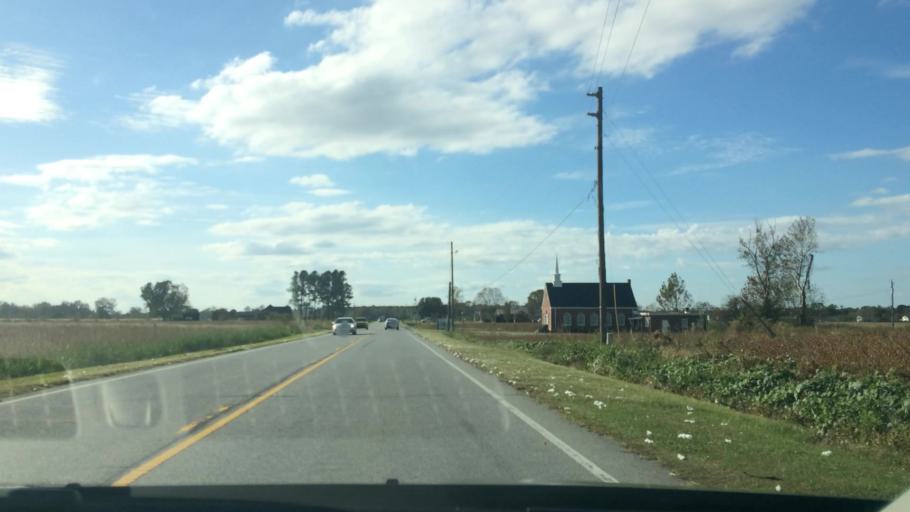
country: US
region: North Carolina
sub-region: Greene County
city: Snow Hill
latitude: 35.4394
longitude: -77.8044
